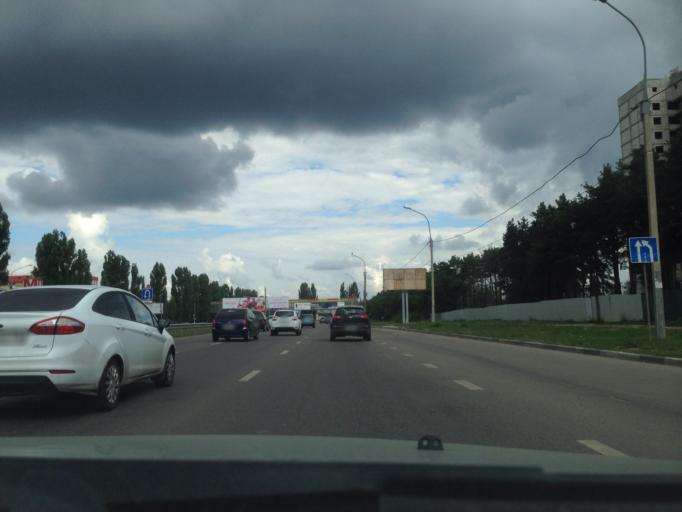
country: RU
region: Voronezj
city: Podgornoye
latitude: 51.7198
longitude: 39.1799
